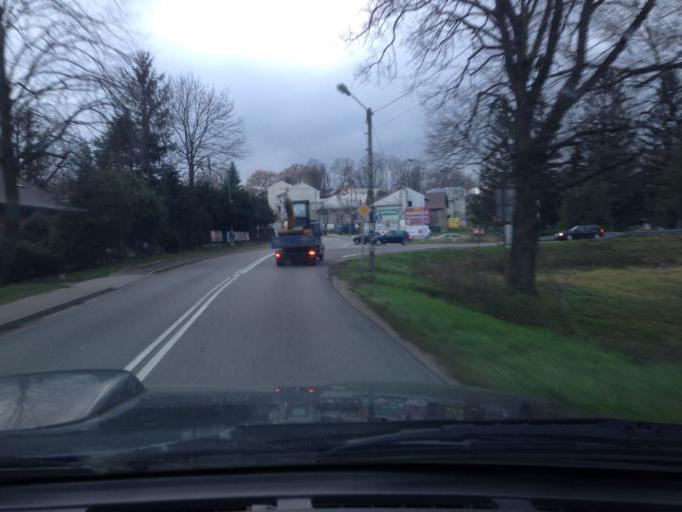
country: PL
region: Subcarpathian Voivodeship
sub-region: Powiat jasielski
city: Nowy Zmigrod
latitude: 49.6076
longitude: 21.5271
